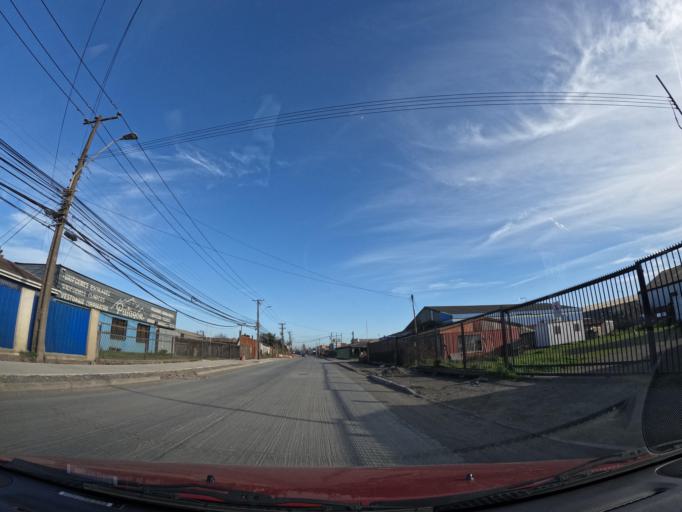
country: CL
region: Biobio
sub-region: Provincia de Concepcion
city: Talcahuano
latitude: -36.7604
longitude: -73.0809
